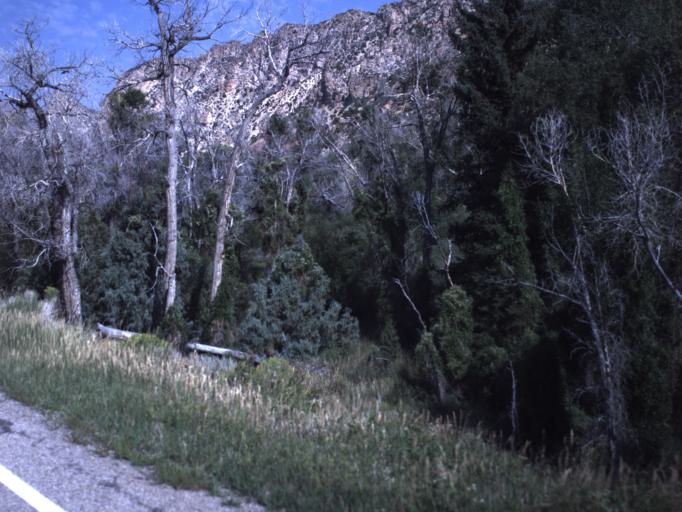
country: US
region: Utah
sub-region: Daggett County
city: Manila
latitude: 40.9203
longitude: -109.6987
